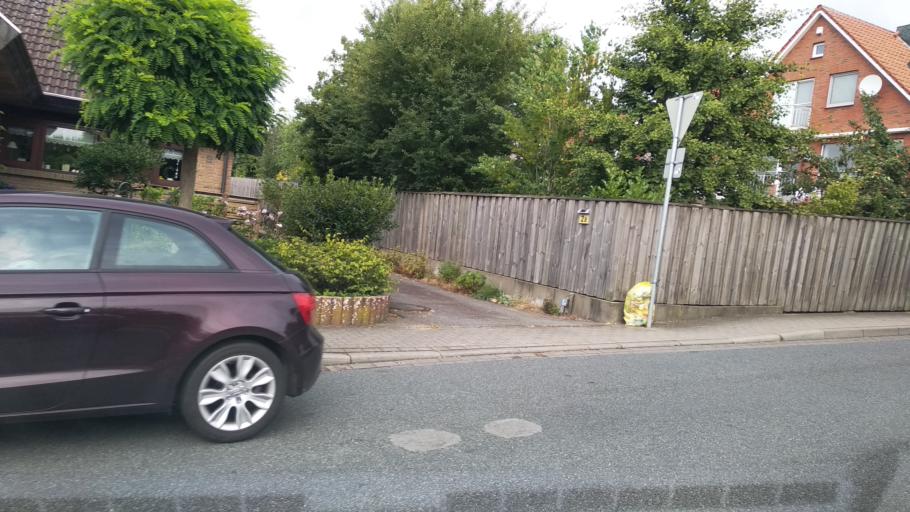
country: DE
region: Schleswig-Holstein
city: Schleswig
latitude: 54.5172
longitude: 9.5799
